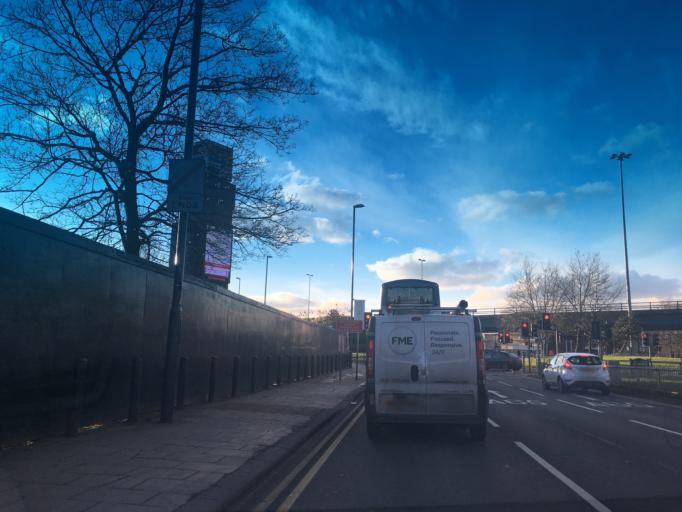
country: GB
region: England
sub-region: City and Borough of Leeds
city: Leeds
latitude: 53.7970
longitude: -1.5591
